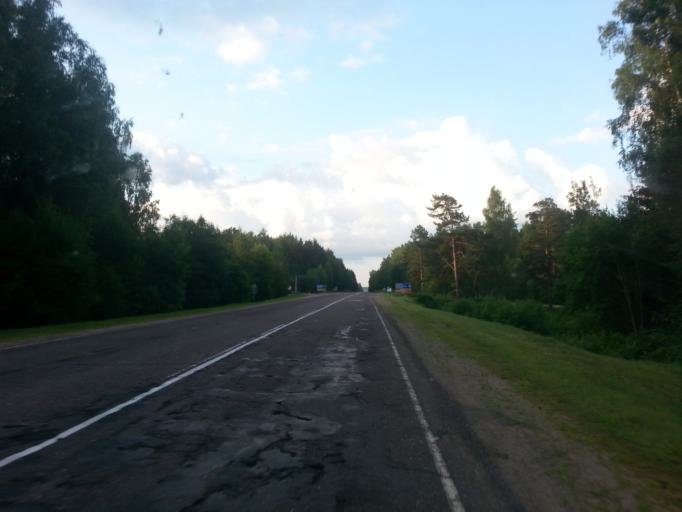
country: BY
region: Minsk
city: Kryvichy
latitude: 54.5901
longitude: 27.1930
